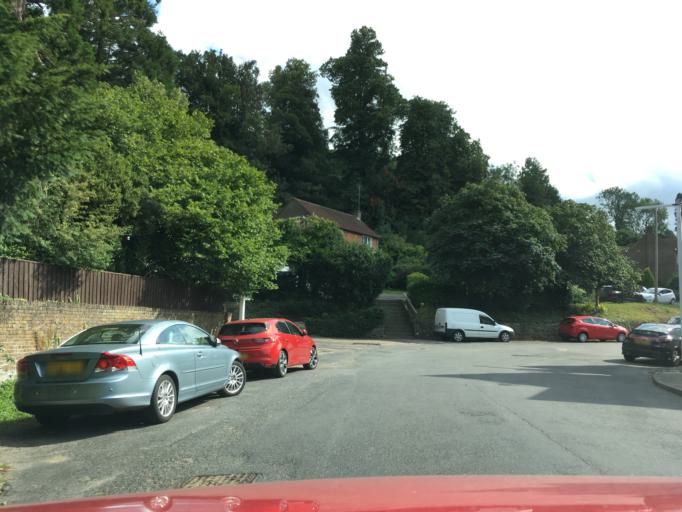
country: GB
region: England
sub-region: Kent
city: Maidstone
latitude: 51.2409
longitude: 0.5179
